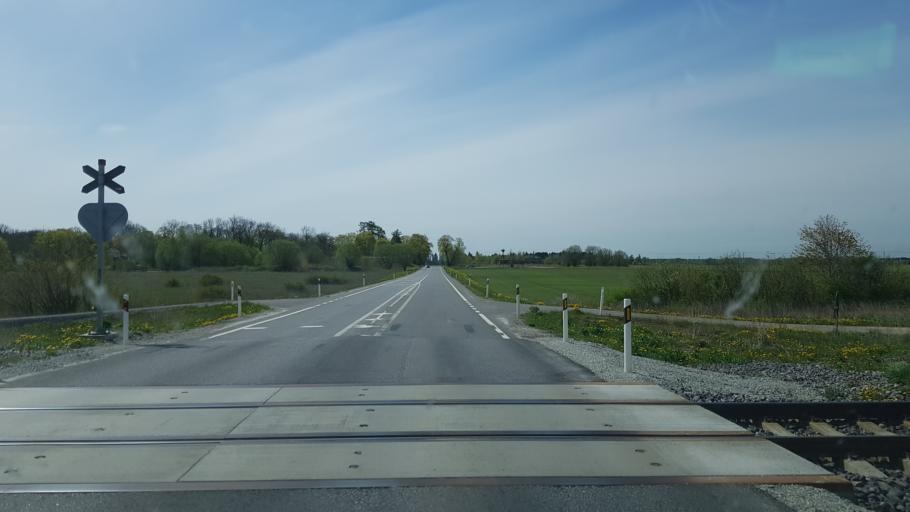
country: EE
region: Ida-Virumaa
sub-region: Johvi vald
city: Johvi
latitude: 59.3576
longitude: 27.3509
